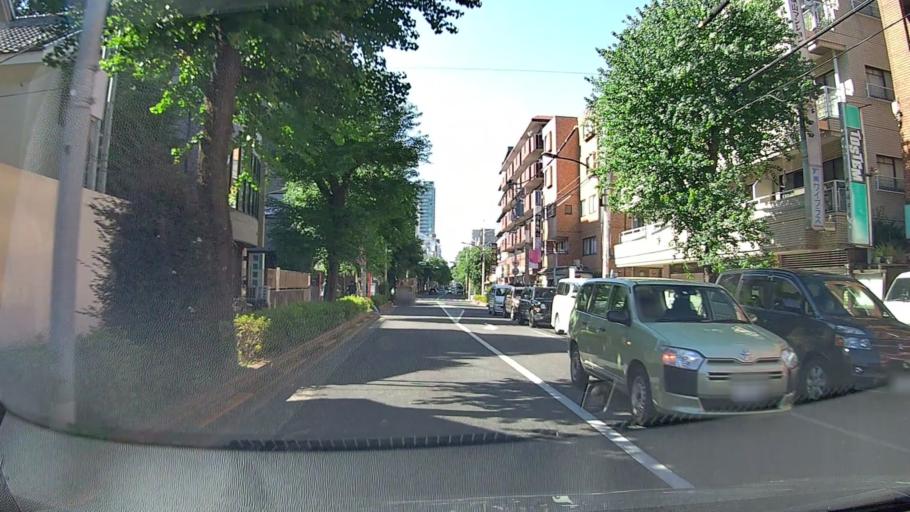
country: JP
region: Saitama
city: Wako
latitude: 35.7506
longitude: 139.5925
